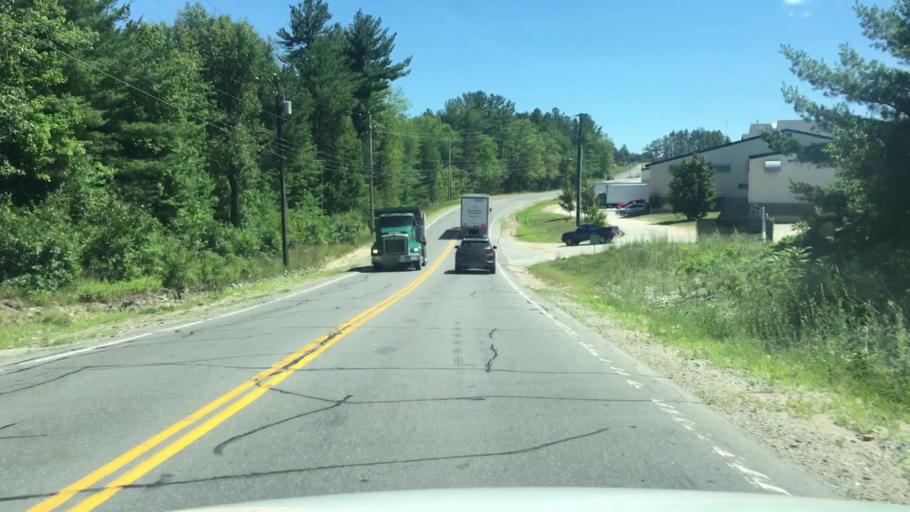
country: US
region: New Hampshire
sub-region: Merrimack County
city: Hooksett
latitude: 43.1146
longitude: -71.4763
